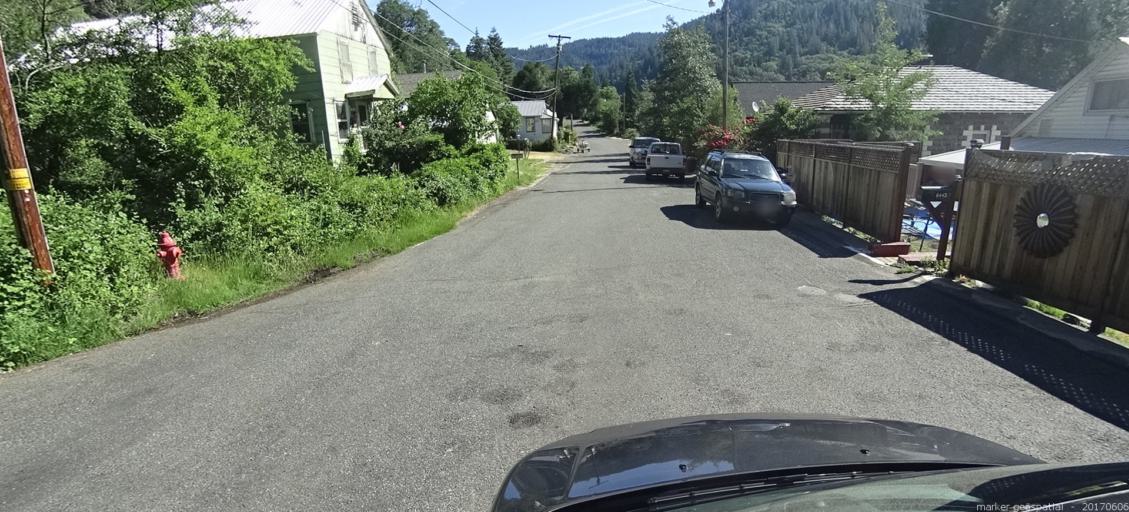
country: US
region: California
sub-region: Siskiyou County
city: Dunsmuir
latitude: 41.1992
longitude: -122.2757
